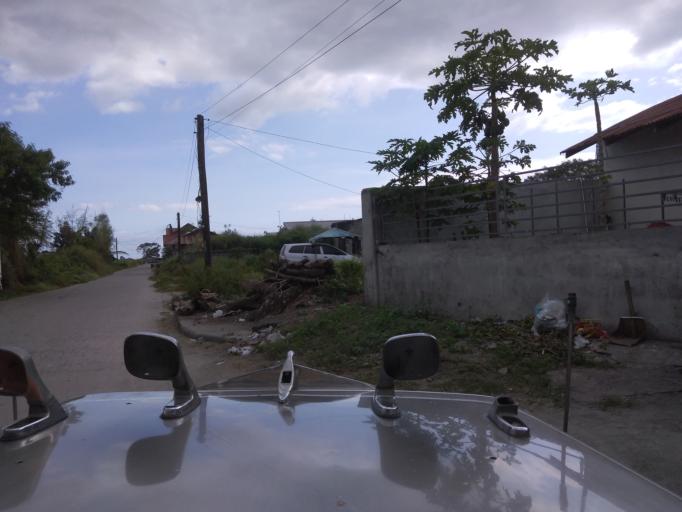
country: PH
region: Central Luzon
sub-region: Province of Pampanga
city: Pandacaqui
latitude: 15.1894
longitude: 120.6507
